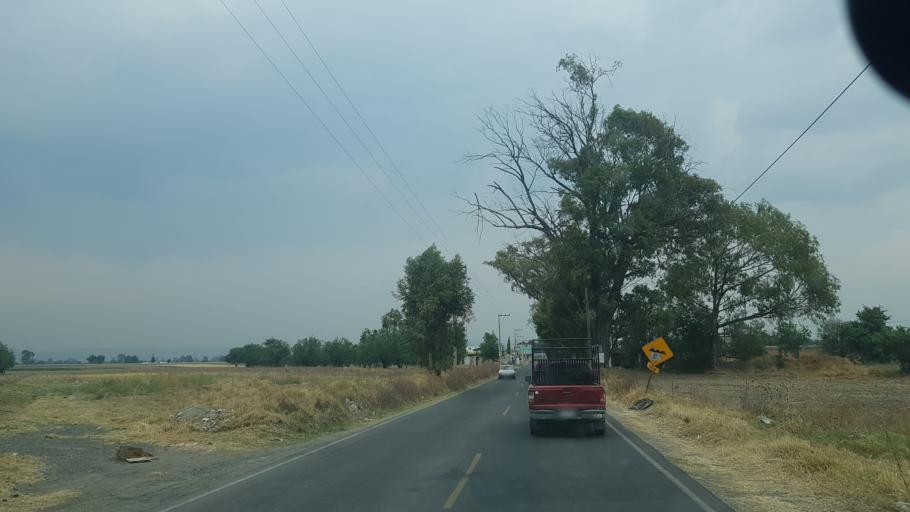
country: MX
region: Puebla
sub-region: Huejotzingo
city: San Mateo Capultitlan
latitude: 19.2010
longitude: -98.4352
